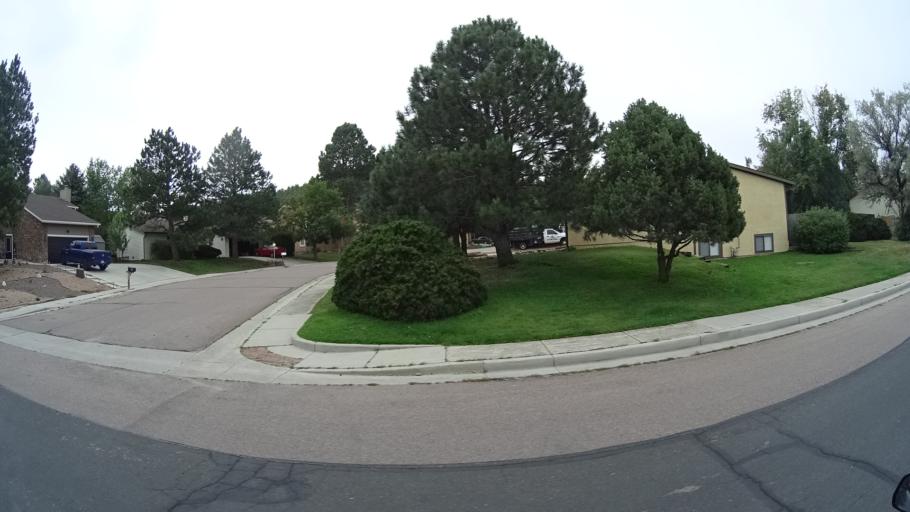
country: US
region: Colorado
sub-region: El Paso County
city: Air Force Academy
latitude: 38.9248
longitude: -104.8096
